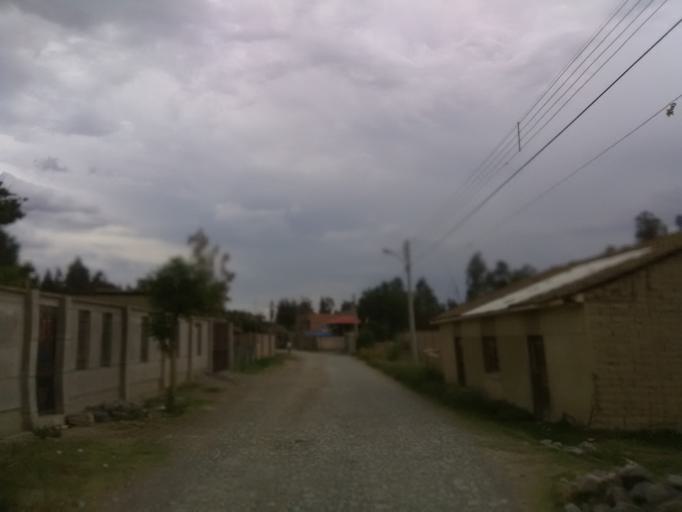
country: BO
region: Cochabamba
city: Cochabamba
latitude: -17.3527
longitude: -66.2251
